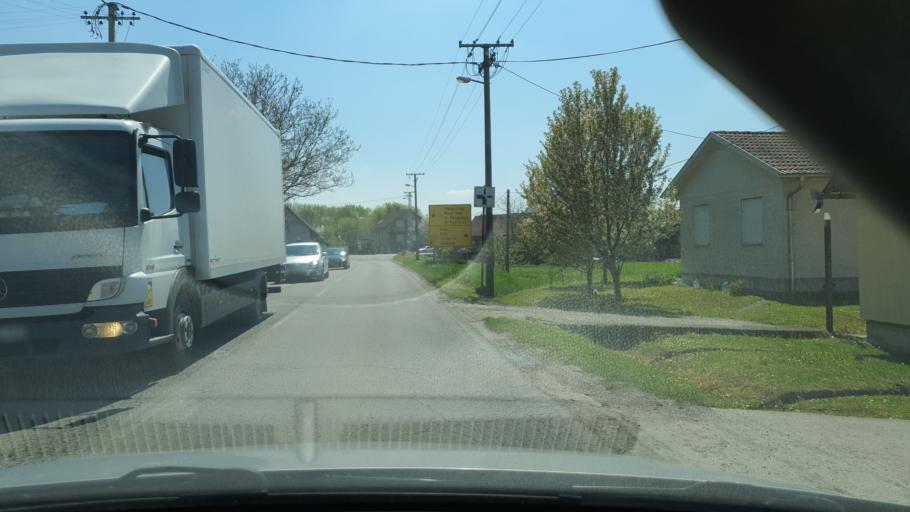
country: RS
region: Autonomna Pokrajina Vojvodina
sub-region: Zapadnobacki Okrug
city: Odzaci
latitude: 45.4503
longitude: 19.3317
